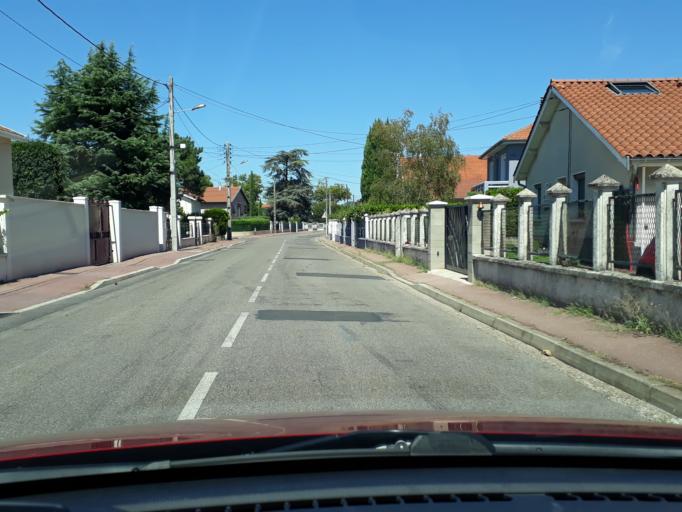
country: FR
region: Rhone-Alpes
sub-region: Departement du Rhone
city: Saint-Priest
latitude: 45.6994
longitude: 4.9267
